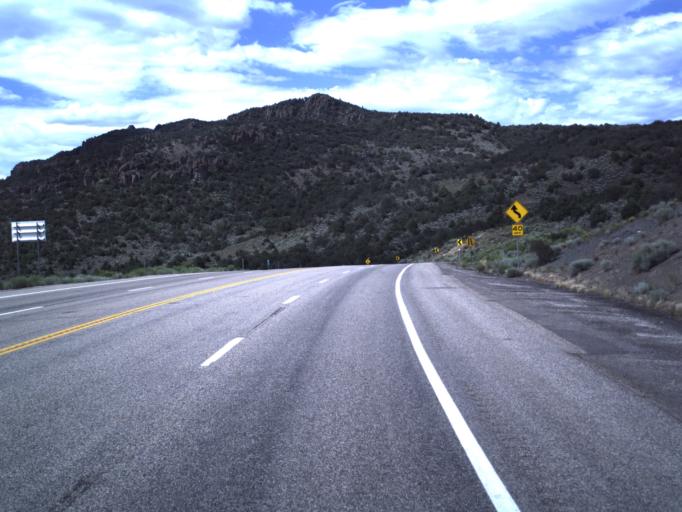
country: US
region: Utah
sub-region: Garfield County
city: Panguitch
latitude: 38.0306
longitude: -112.5309
